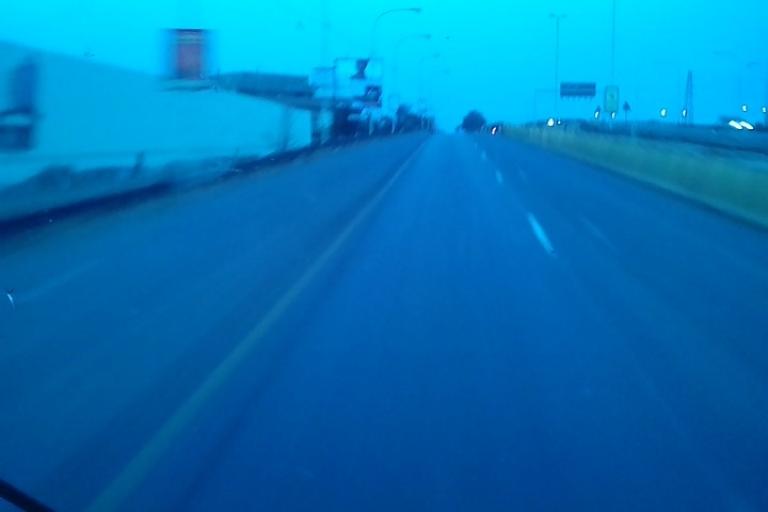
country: ZA
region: Gauteng
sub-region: City of Johannesburg Metropolitan Municipality
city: Johannesburg
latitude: -26.2136
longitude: 28.0193
